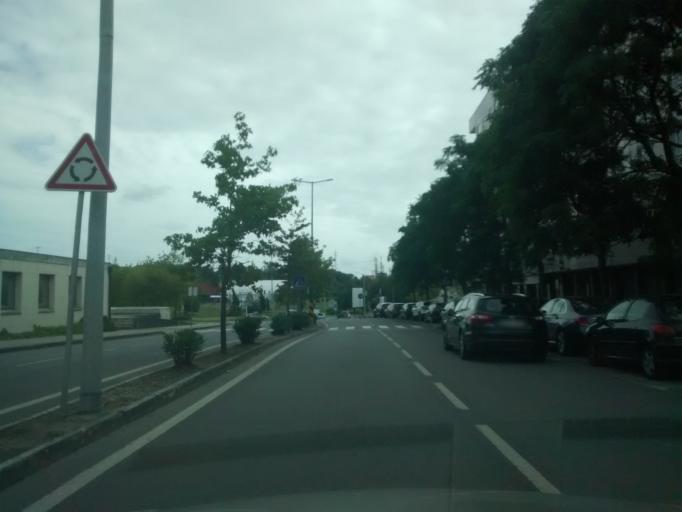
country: PT
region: Aveiro
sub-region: Aveiro
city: Aveiro
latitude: 40.6400
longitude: -8.6406
